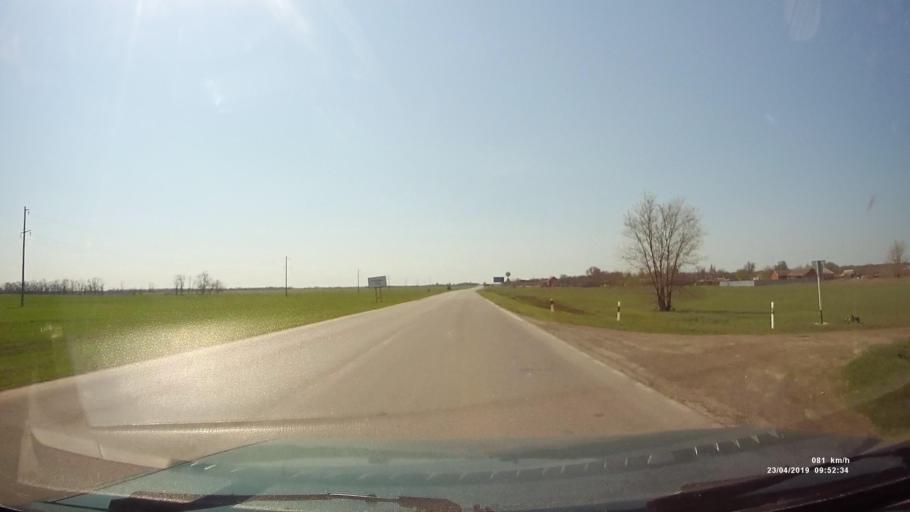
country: RU
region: Rostov
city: Orlovskiy
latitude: 46.8430
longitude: 42.0464
